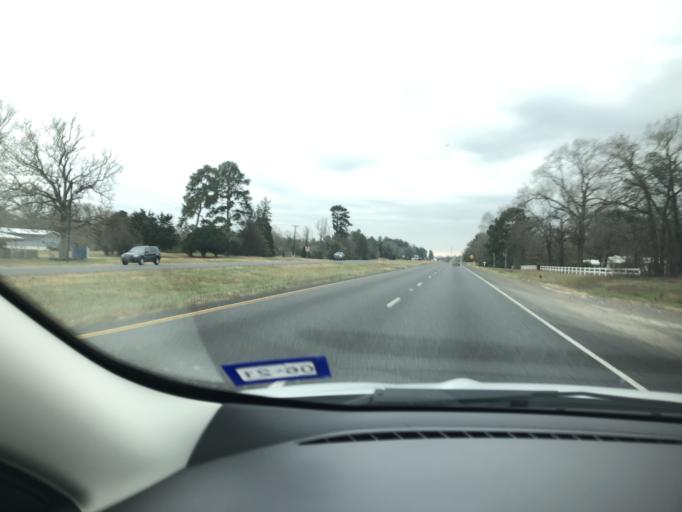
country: US
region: Texas
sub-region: Angelina County
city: Redland
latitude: 31.5010
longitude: -94.7085
